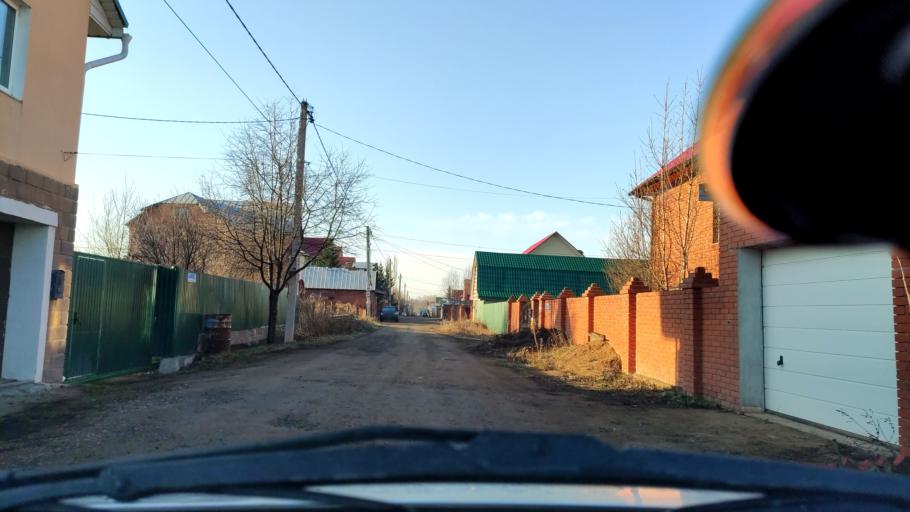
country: RU
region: Bashkortostan
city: Mikhaylovka
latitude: 54.8055
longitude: 55.9412
